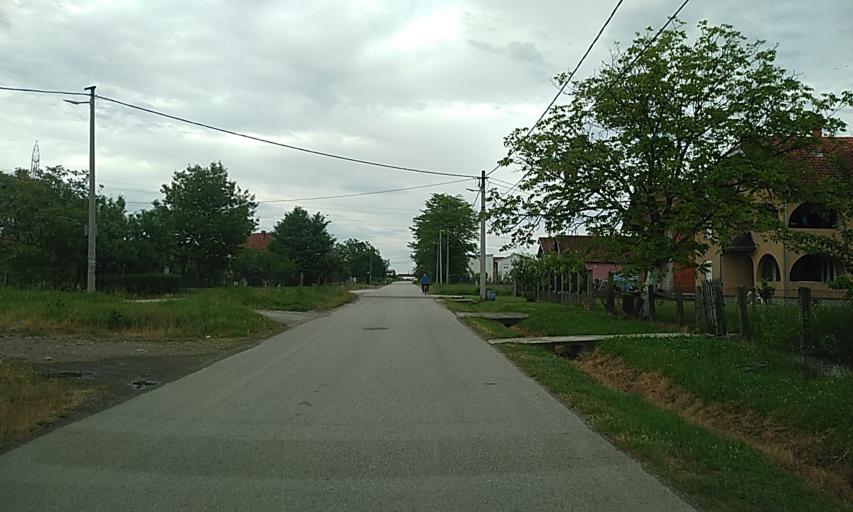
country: RS
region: Central Serbia
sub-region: Rasinski Okrug
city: Krusevac
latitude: 43.5917
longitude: 21.2786
